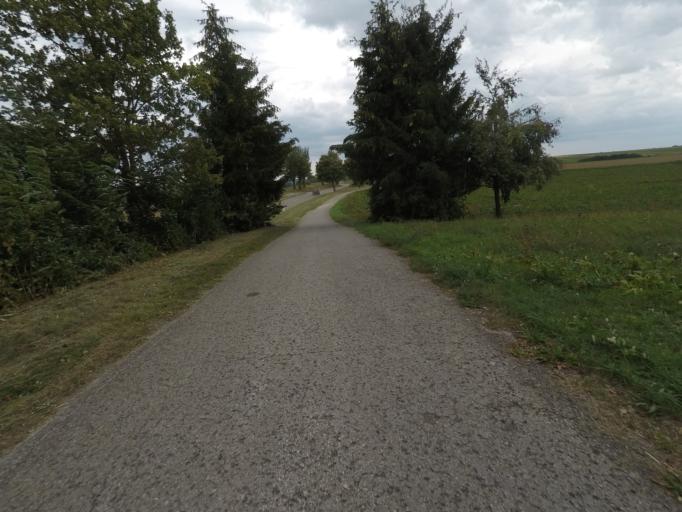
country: DE
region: Baden-Wuerttemberg
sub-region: Regierungsbezirk Stuttgart
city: Herrenberg
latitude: 48.5532
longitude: 8.9061
